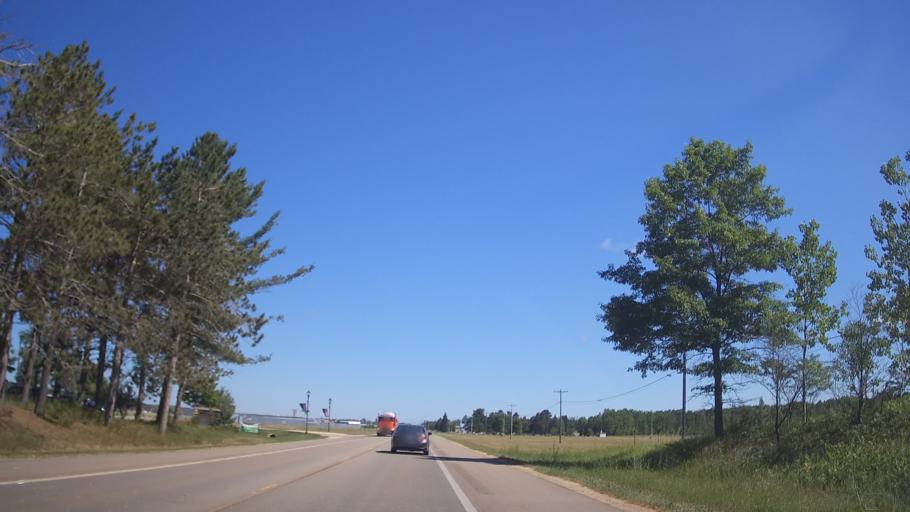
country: US
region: Michigan
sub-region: Cheboygan County
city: Indian River
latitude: 45.5570
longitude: -84.7844
